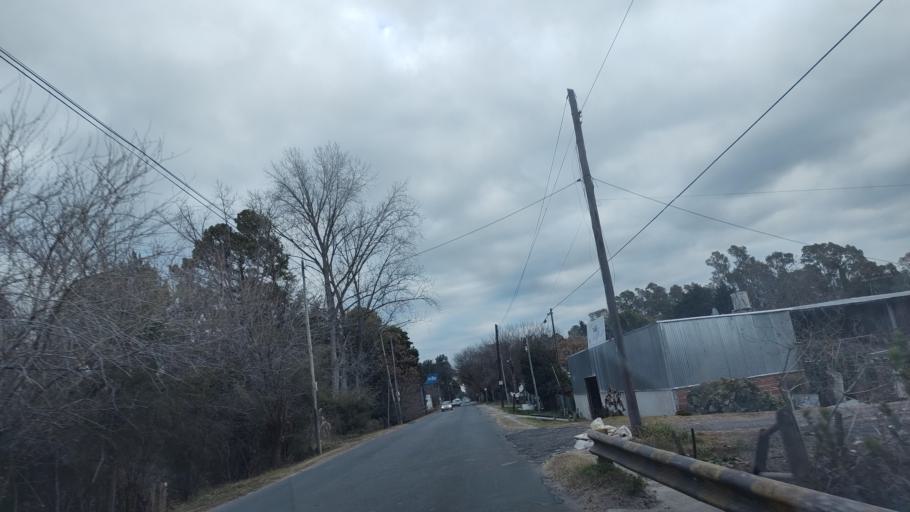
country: AR
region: Buenos Aires
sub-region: Partido de La Plata
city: La Plata
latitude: -34.8630
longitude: -58.0902
